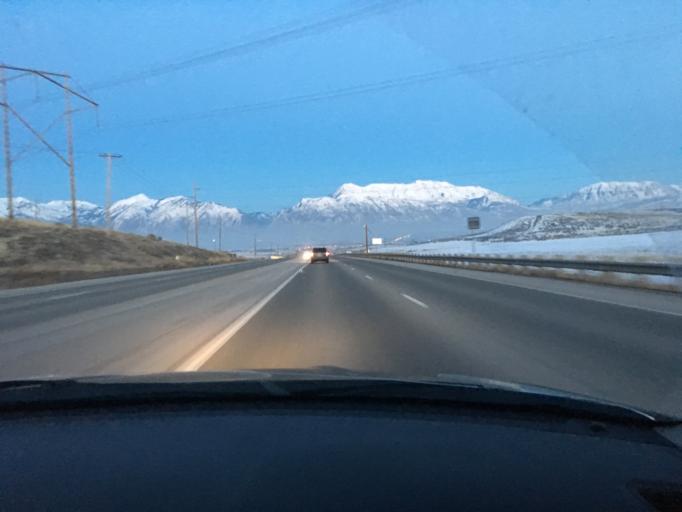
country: US
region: Utah
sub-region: Utah County
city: Saratoga Springs
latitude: 40.3838
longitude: -111.9551
